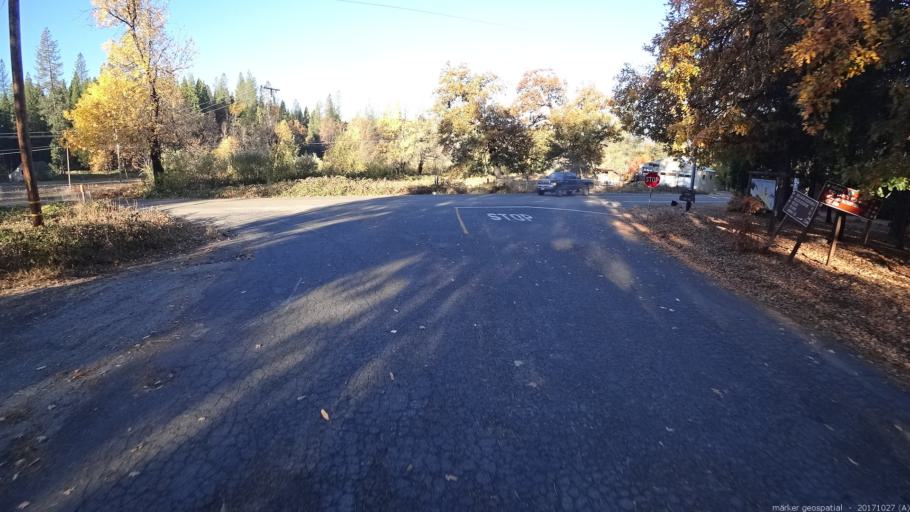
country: US
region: California
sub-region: Shasta County
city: Burney
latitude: 41.0142
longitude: -121.9057
